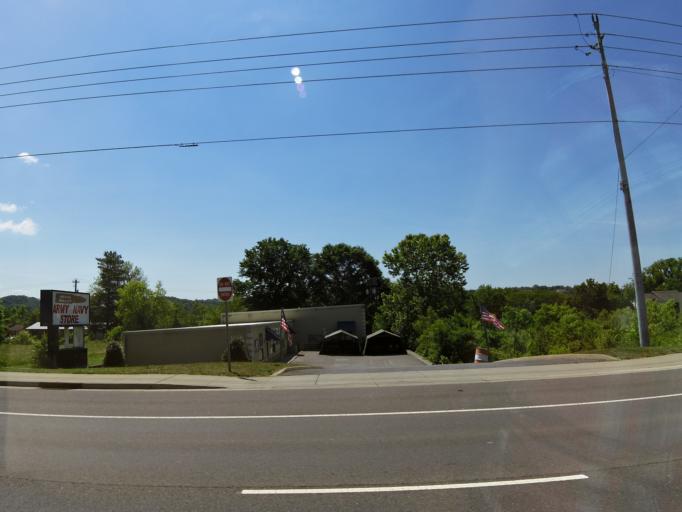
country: US
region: Tennessee
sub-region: Sevier County
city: Sevierville
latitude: 35.9125
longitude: -83.5812
